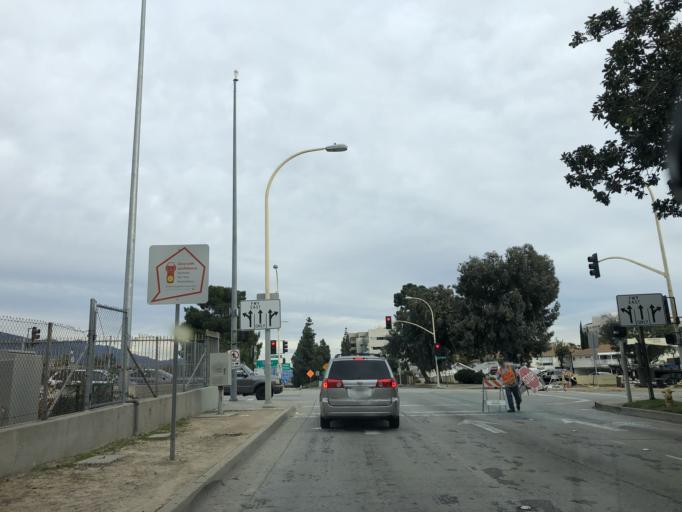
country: US
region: California
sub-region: Los Angeles County
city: Pasadena
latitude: 34.1514
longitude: -118.1465
